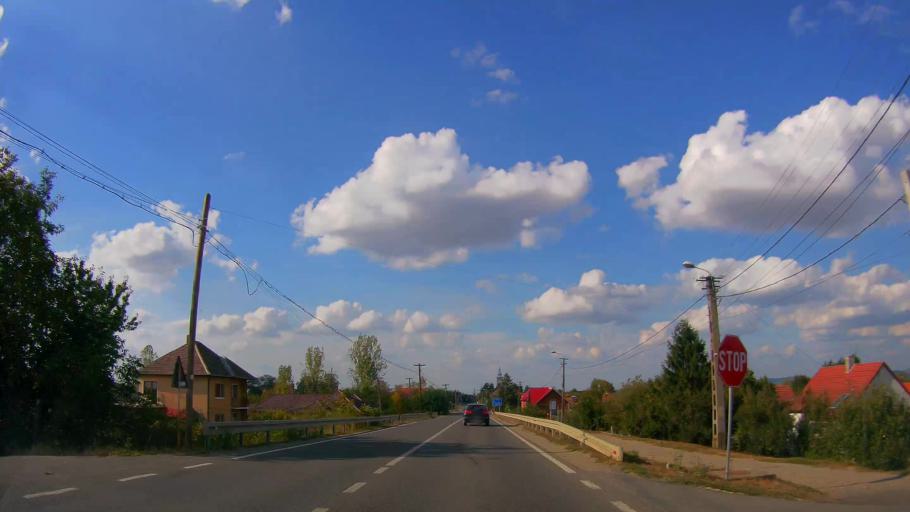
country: RO
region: Satu Mare
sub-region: Comuna Turulung
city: Turulung
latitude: 47.9297
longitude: 23.0849
